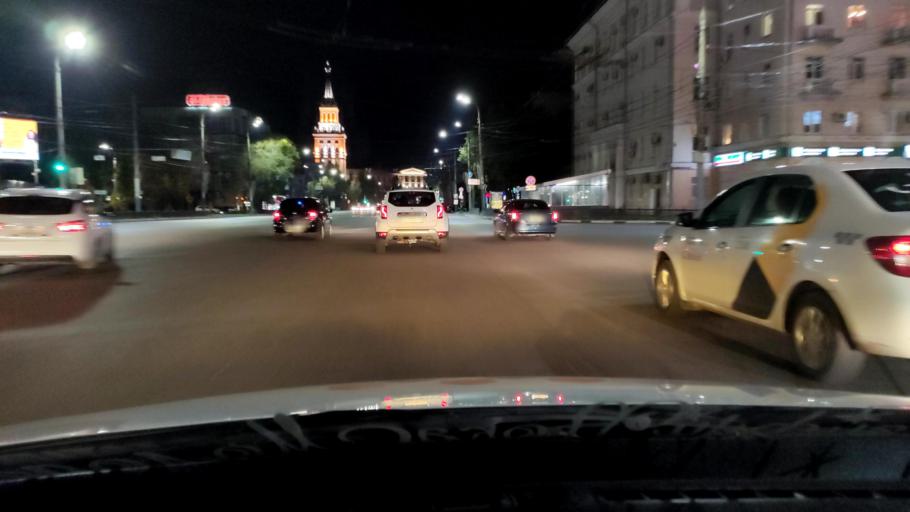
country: RU
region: Voronezj
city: Voronezh
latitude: 51.6556
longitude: 39.1879
